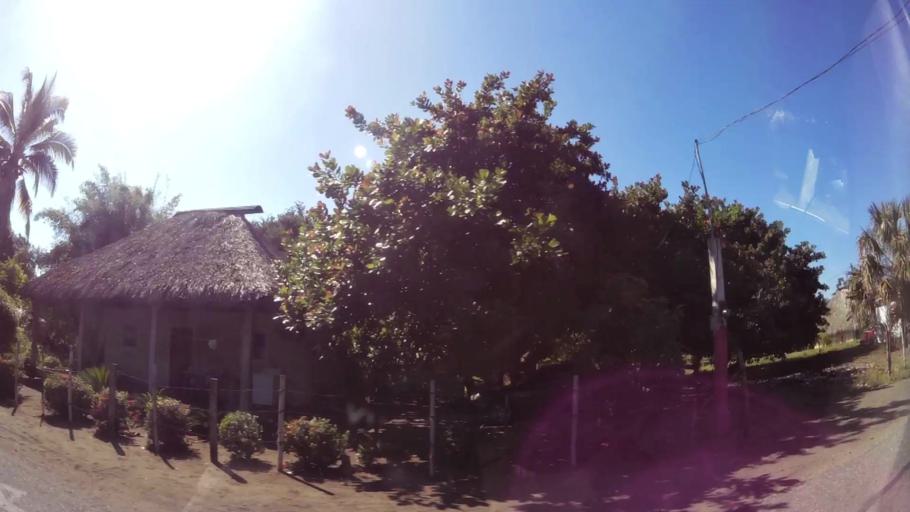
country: GT
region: Santa Rosa
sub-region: Municipio de Taxisco
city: Taxisco
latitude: 13.9086
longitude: -90.5208
